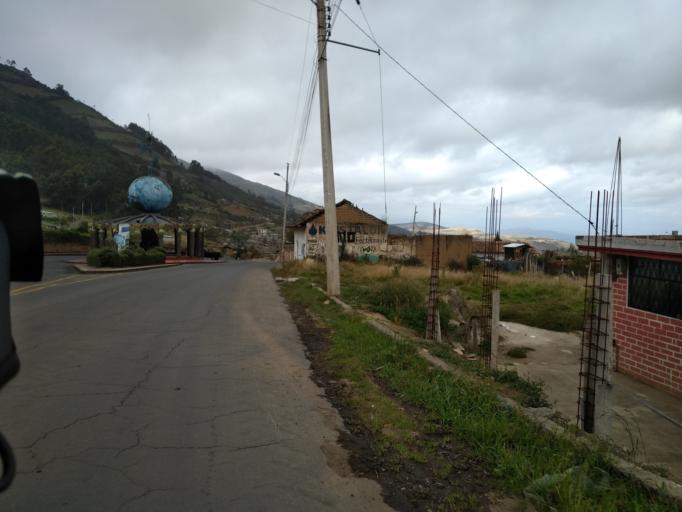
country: EC
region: Carchi
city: El Angel
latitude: 0.6253
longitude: -77.9345
